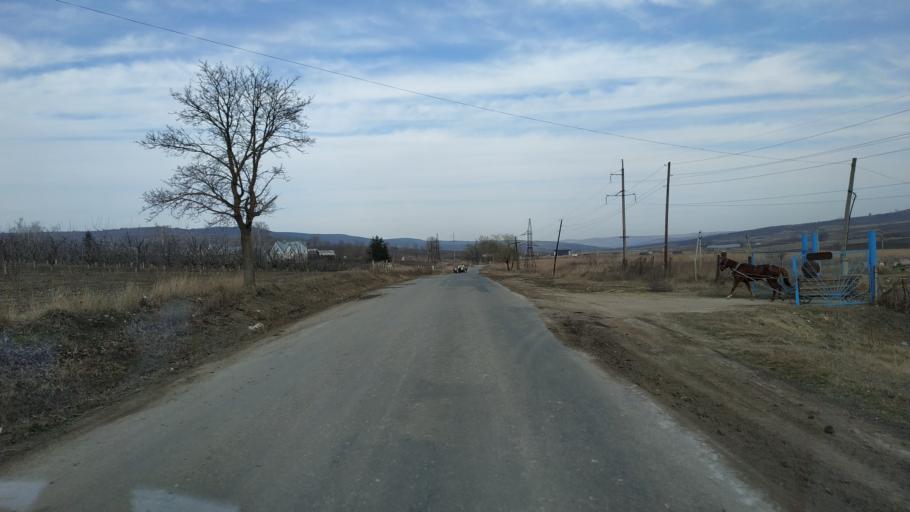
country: MD
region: Nisporeni
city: Nisporeni
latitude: 47.0849
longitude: 28.1412
